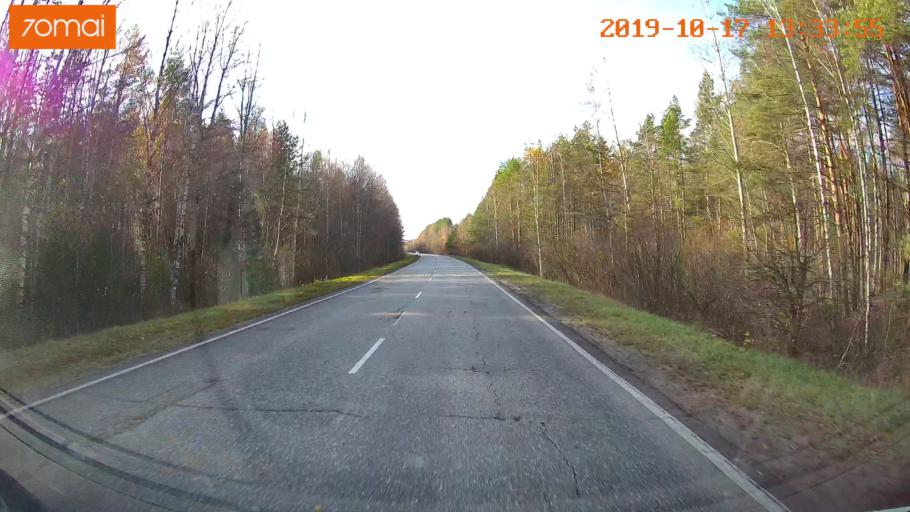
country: RU
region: Vladimir
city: Velikodvorskiy
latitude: 55.1444
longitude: 40.7296
